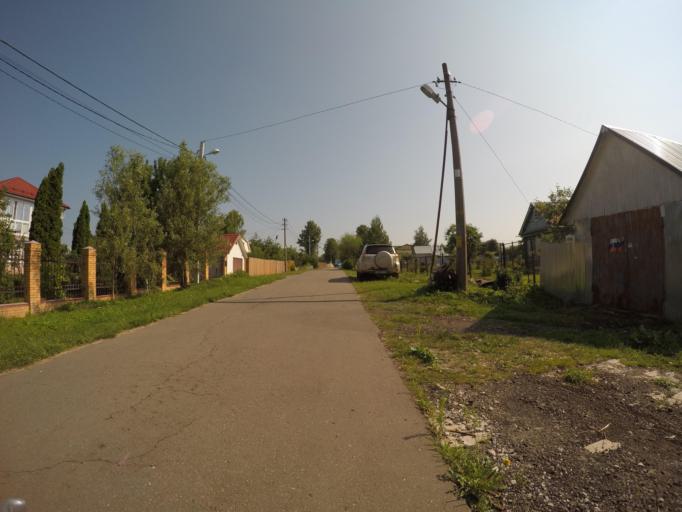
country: RU
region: Moskovskaya
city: Rechitsy
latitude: 55.6101
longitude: 38.5341
